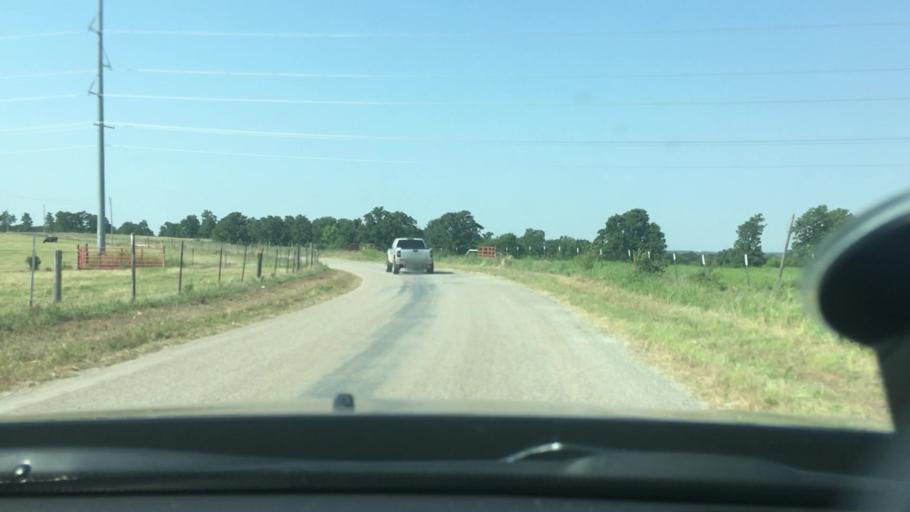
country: US
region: Oklahoma
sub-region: Garvin County
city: Lindsay
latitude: 34.7752
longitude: -97.6114
